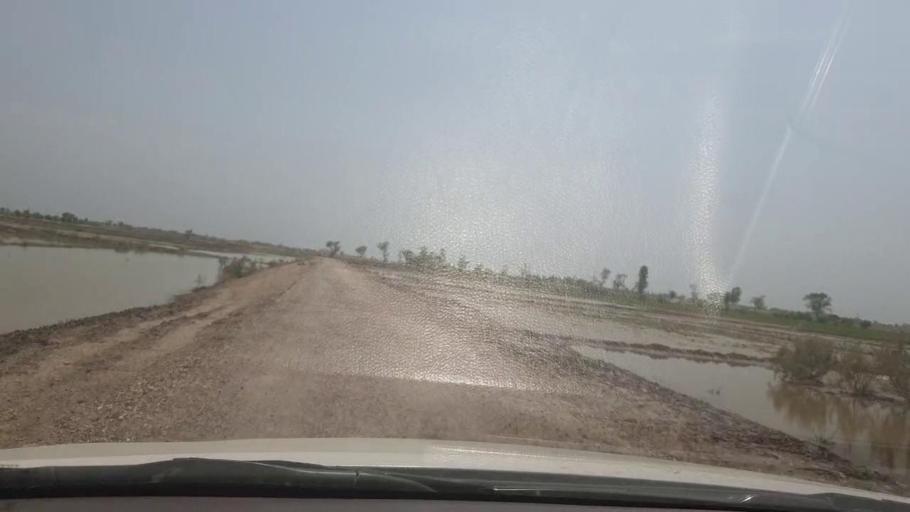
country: PK
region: Sindh
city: Shikarpur
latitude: 28.0334
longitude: 68.5735
